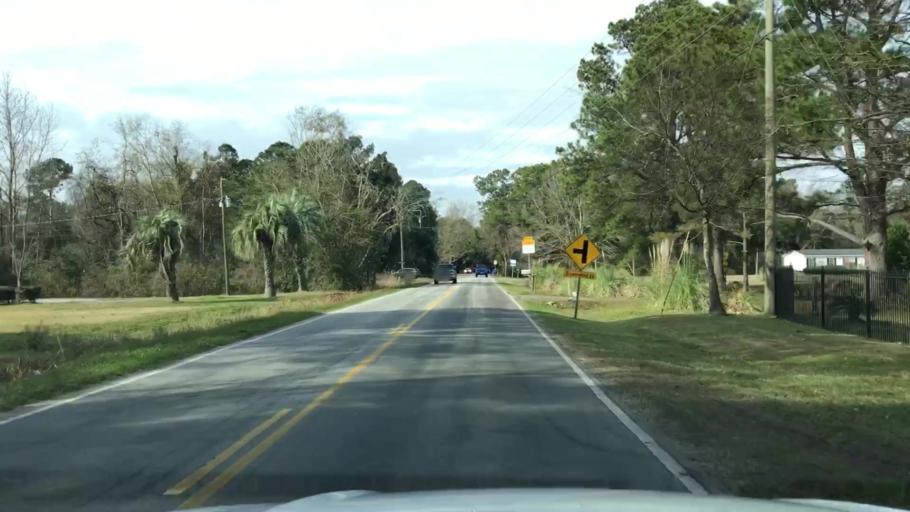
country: US
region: South Carolina
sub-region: Charleston County
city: Shell Point
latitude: 32.7671
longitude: -80.0696
